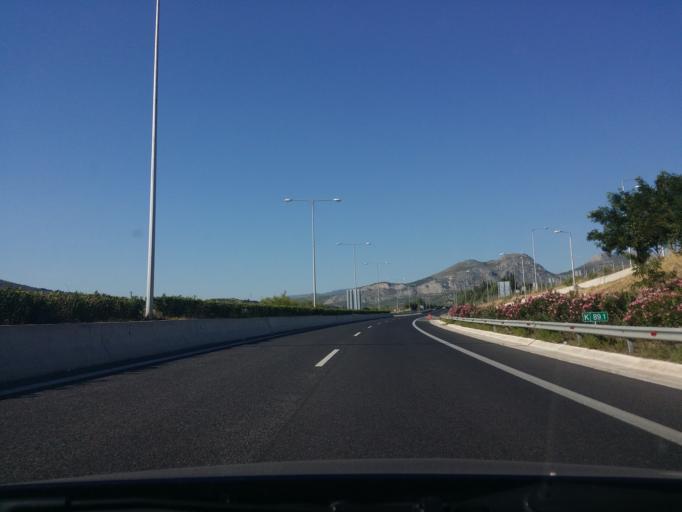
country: GR
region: Peloponnese
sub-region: Nomos Korinthias
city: Arkhaia Korinthos
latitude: 37.8931
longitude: 22.8967
